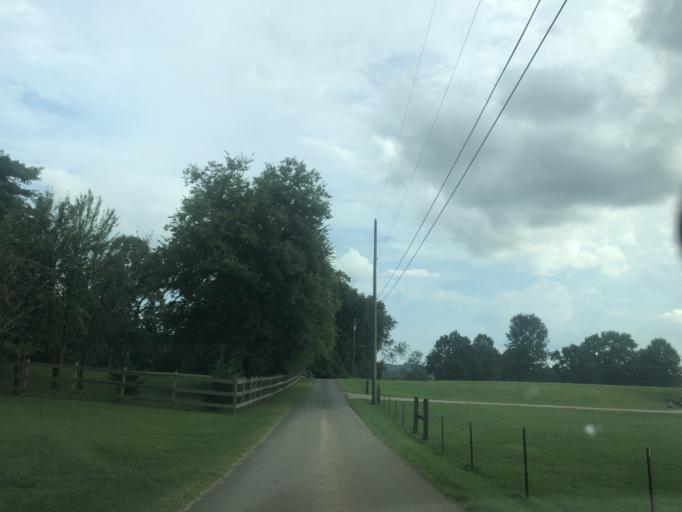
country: US
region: Tennessee
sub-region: Davidson County
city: Lakewood
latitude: 36.1706
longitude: -86.6247
